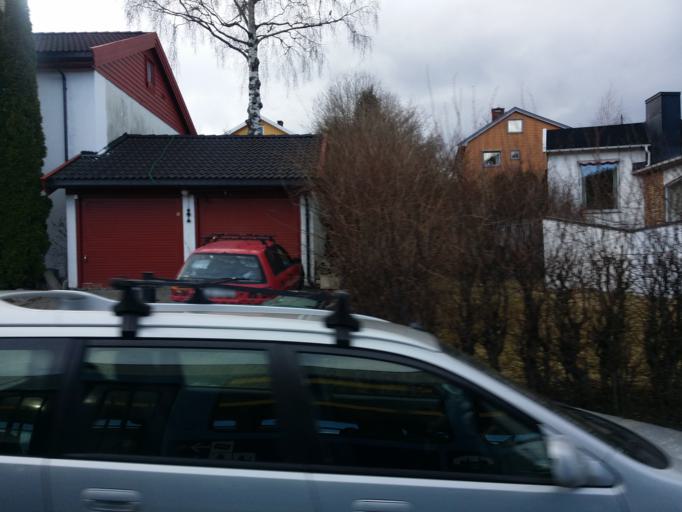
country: NO
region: Oslo
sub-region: Oslo
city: Oslo
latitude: 59.9564
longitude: 10.7857
